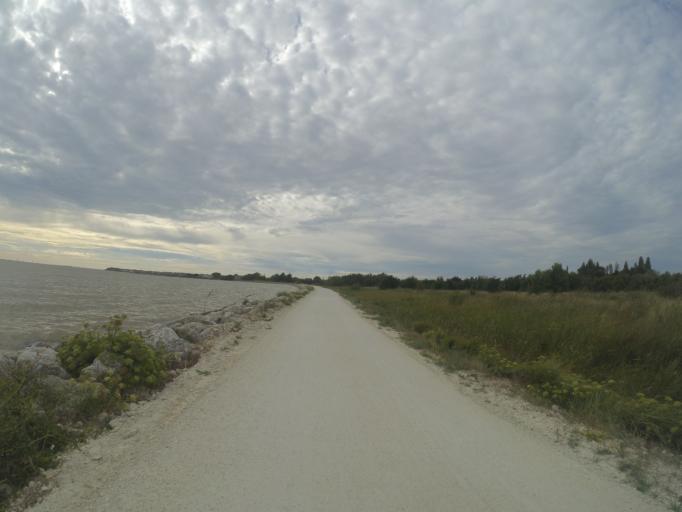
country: FR
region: Poitou-Charentes
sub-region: Departement de la Charente-Maritime
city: Meschers-sur-Gironde
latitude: 45.5496
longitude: -0.9154
